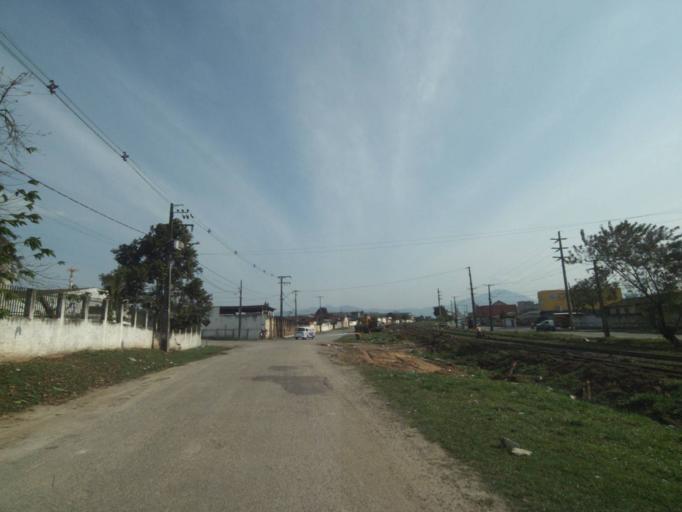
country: BR
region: Parana
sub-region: Paranagua
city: Paranagua
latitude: -25.5347
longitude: -48.5326
